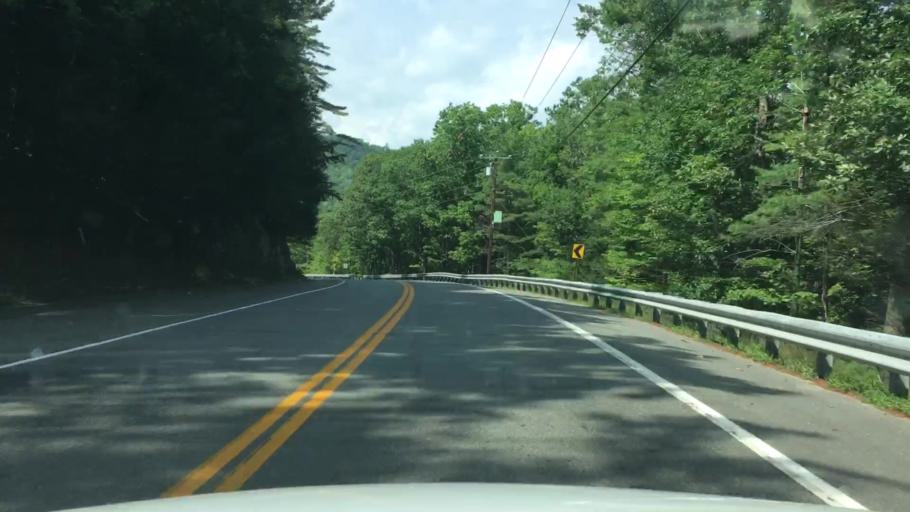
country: US
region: Maine
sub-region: Oxford County
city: Dixfield
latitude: 44.5295
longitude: -70.4666
